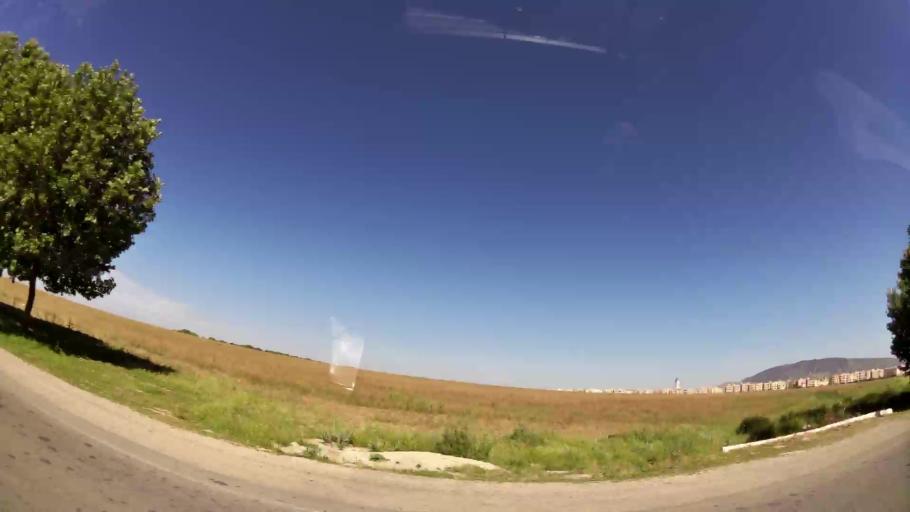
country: MA
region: Fes-Boulemane
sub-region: Fes
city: Fes
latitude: 34.0037
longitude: -5.0231
